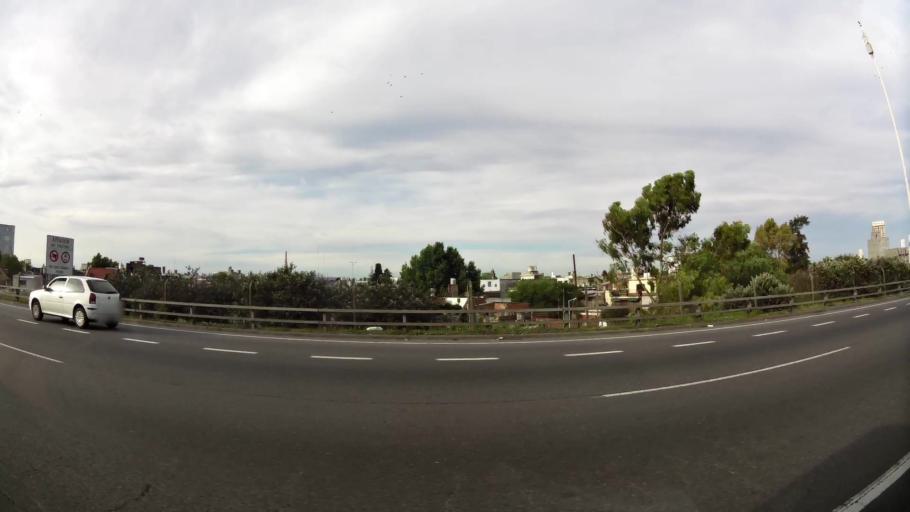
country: AR
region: Buenos Aires
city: Caseros
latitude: -34.6340
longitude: -58.5388
